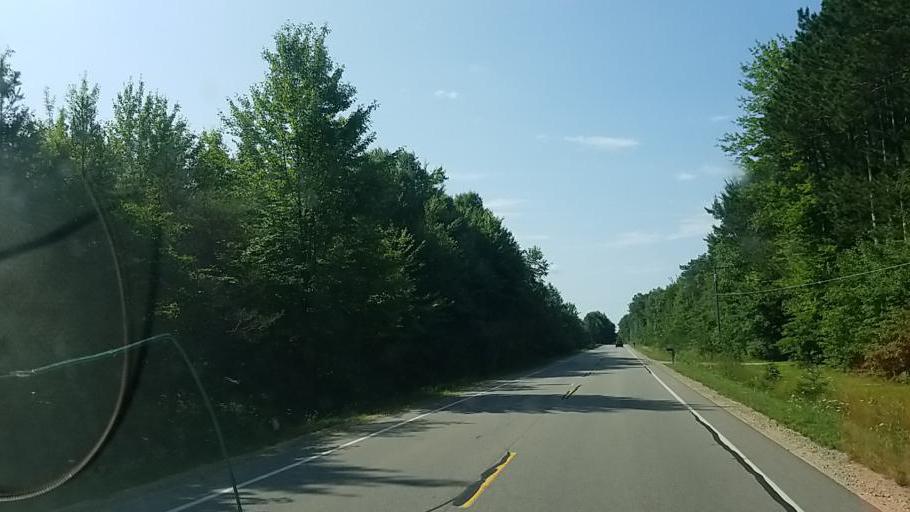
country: US
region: Michigan
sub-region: Muskegon County
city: Whitehall
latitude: 43.3661
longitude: -86.3462
